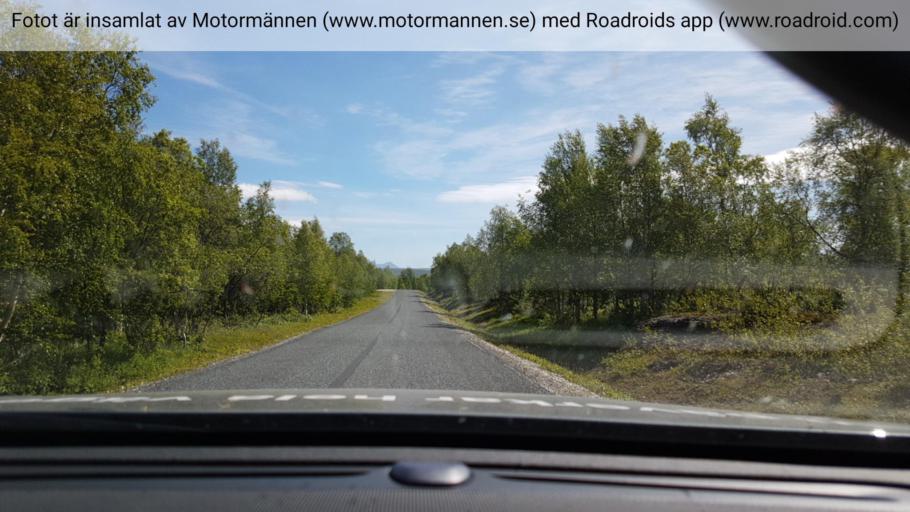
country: NO
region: Nordland
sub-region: Hattfjelldal
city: Hattfjelldal
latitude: 65.3479
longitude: 15.0863
